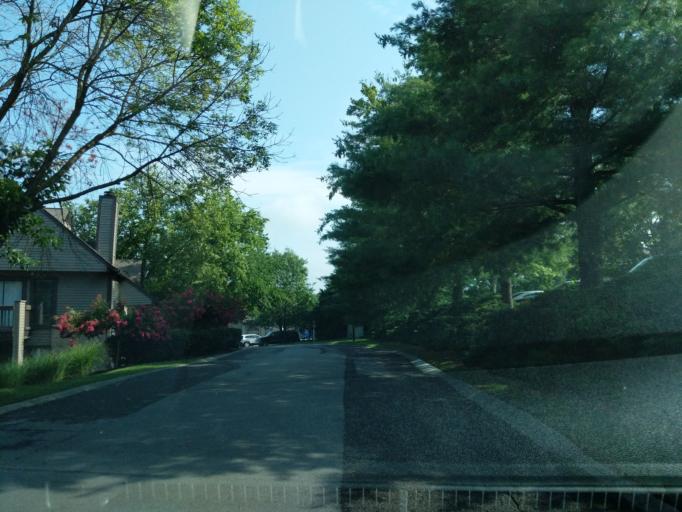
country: US
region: Tennessee
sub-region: Sumner County
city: Hendersonville
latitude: 36.3088
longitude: -86.6537
